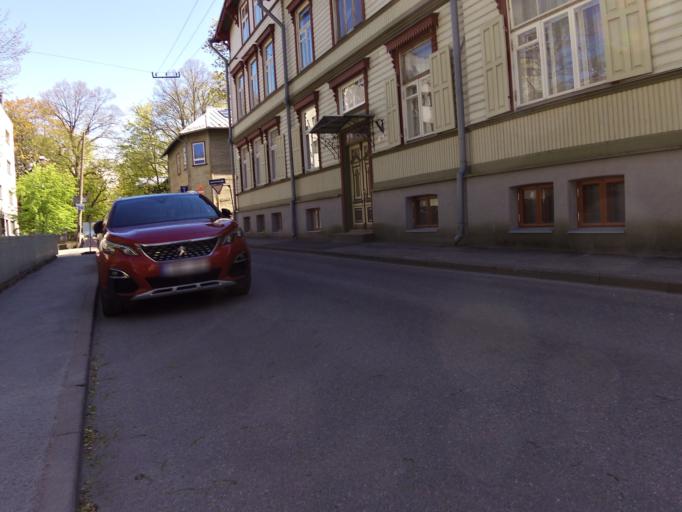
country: EE
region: Harju
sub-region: Tallinna linn
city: Tallinn
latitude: 59.4376
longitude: 24.7783
